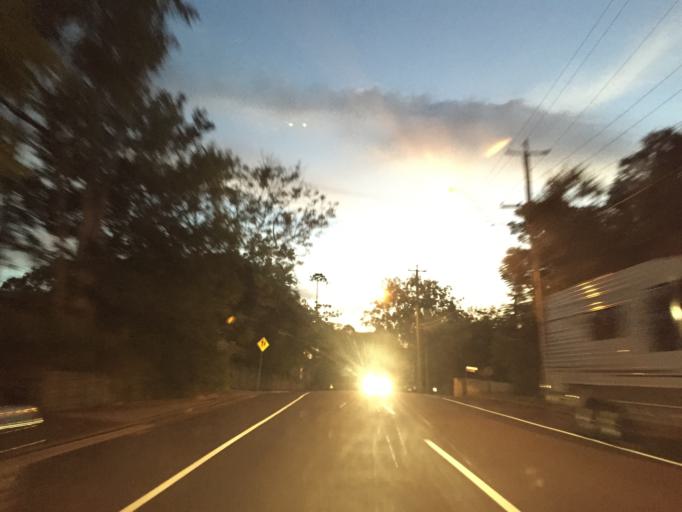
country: AU
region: Queensland
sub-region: Brisbane
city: Taringa
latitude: -27.4499
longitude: 152.9497
